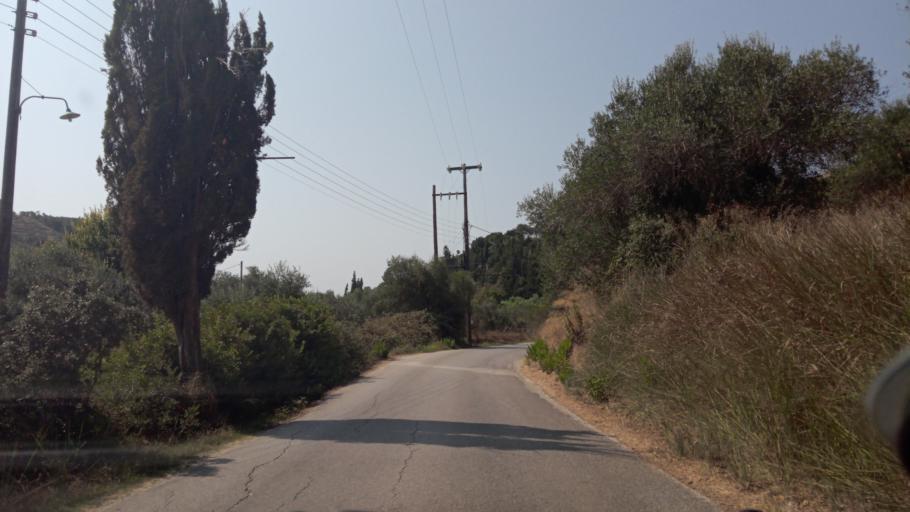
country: GR
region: Ionian Islands
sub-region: Nomos Kerkyras
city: Perivoli
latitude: 39.4018
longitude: 20.0262
